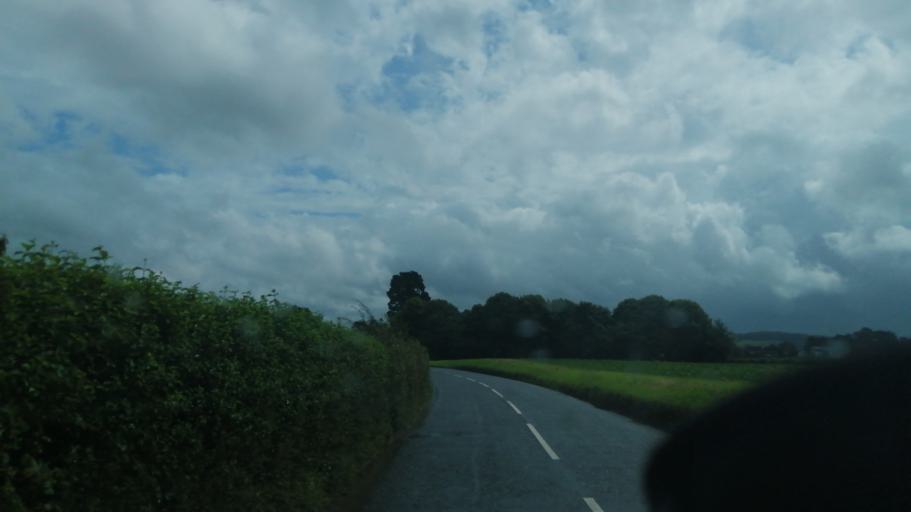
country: GB
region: England
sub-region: Herefordshire
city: Kingstone
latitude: 52.0182
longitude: -2.8494
